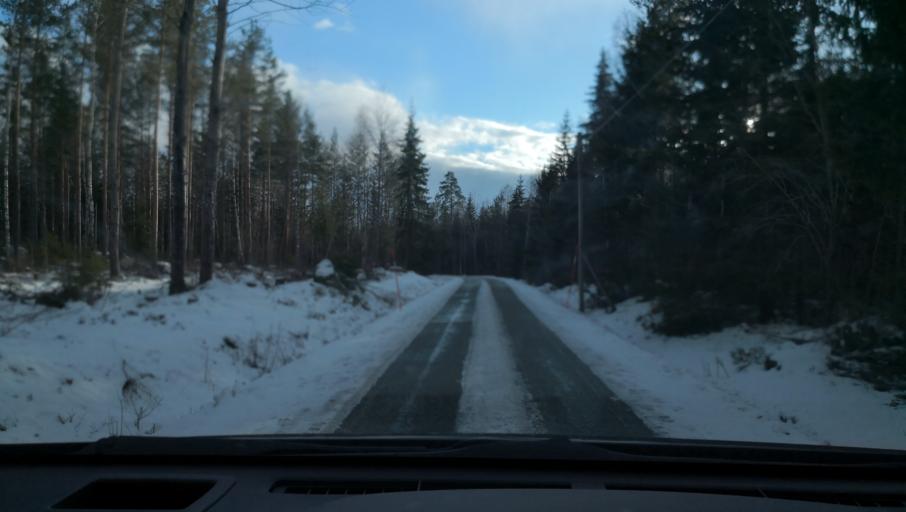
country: SE
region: Uppsala
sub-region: Enkopings Kommun
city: Irsta
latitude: 59.7027
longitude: 16.8699
